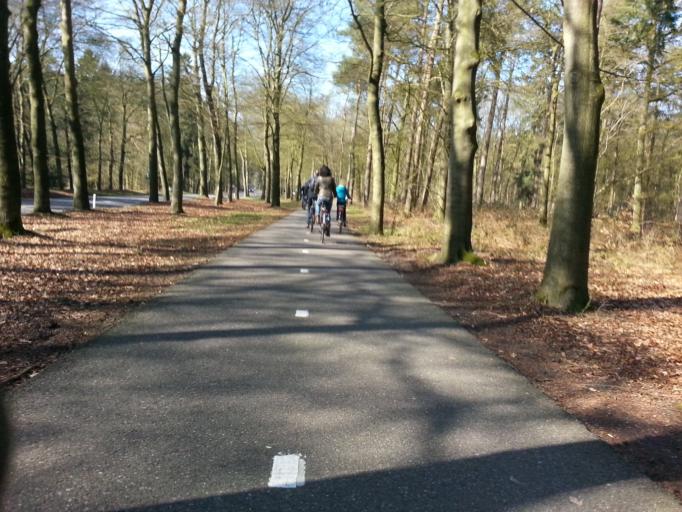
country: NL
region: Utrecht
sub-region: Gemeente Utrechtse Heuvelrug
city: Doorn
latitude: 52.0314
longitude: 5.3736
